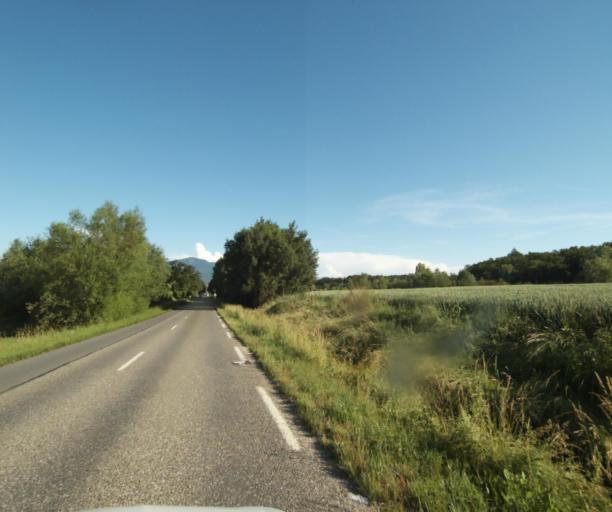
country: FR
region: Rhone-Alpes
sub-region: Departement de la Haute-Savoie
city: Douvaine
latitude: 46.3236
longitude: 6.2937
